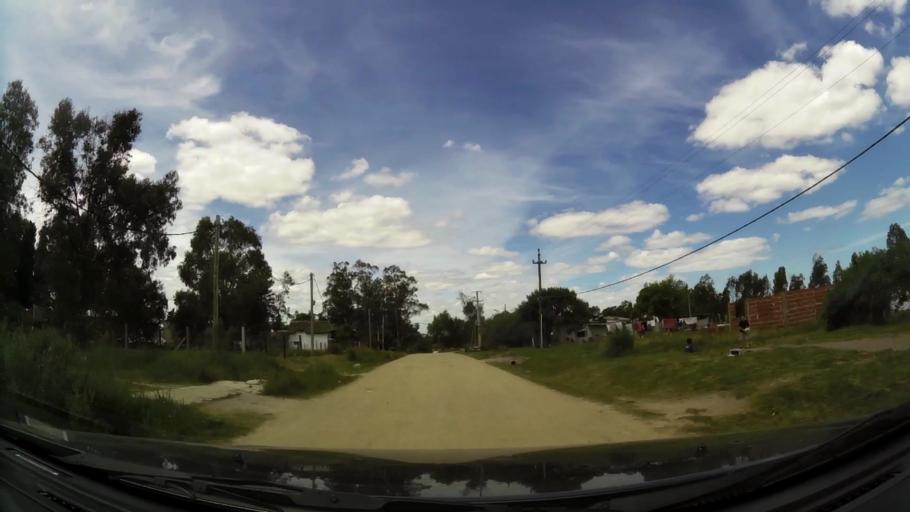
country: UY
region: Canelones
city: Empalme Olmos
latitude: -34.7763
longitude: -55.8842
